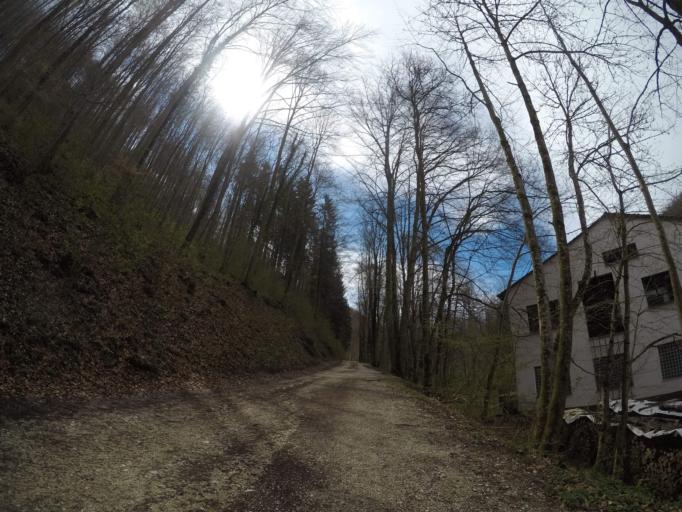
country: DE
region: Baden-Wuerttemberg
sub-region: Regierungsbezirk Stuttgart
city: Wiesensteig
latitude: 48.5613
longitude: 9.5998
